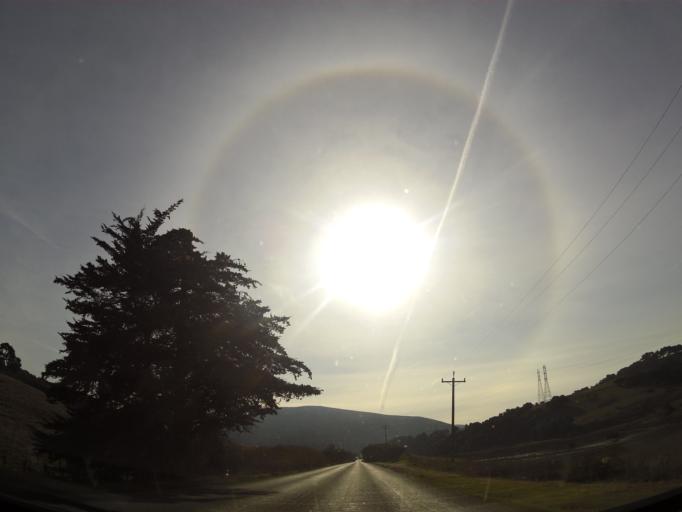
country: US
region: California
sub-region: Monterey County
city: Prunedale
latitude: 36.7819
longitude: -121.6089
